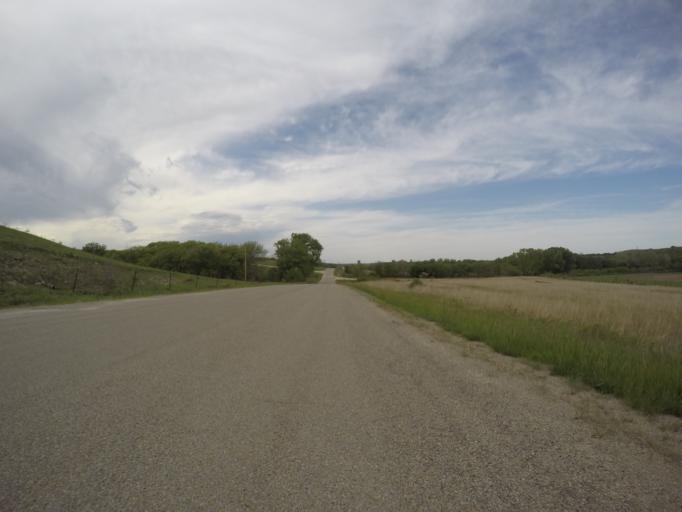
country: US
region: Kansas
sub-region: Riley County
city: Ogden
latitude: 39.0051
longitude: -96.6019
